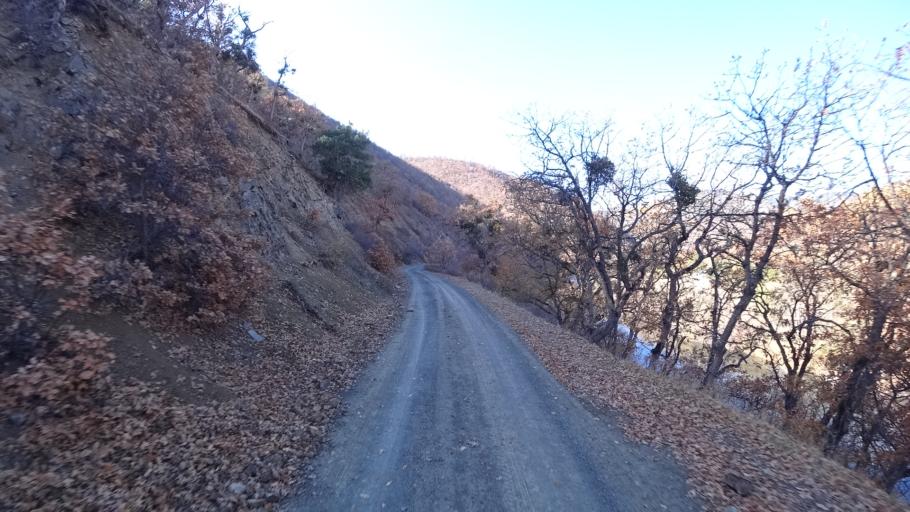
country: US
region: California
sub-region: Siskiyou County
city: Yreka
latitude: 41.8611
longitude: -122.7165
